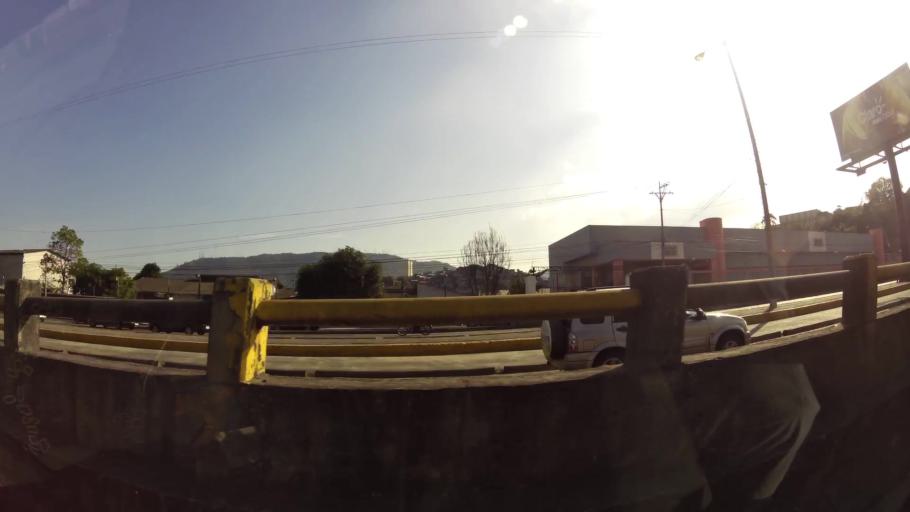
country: EC
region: Guayas
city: Guayaquil
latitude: -2.1507
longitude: -79.9321
